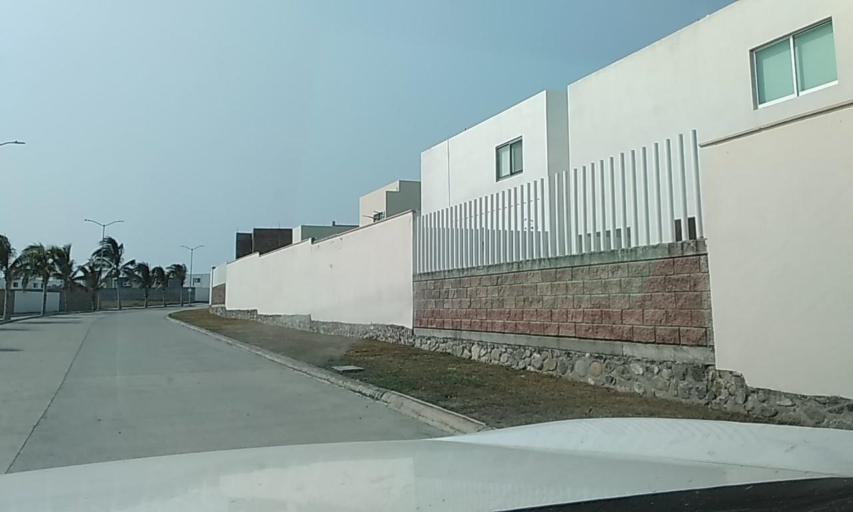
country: MX
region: Veracruz
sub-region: Alvarado
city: Playa de la Libertad
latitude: 19.0422
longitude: -96.0605
